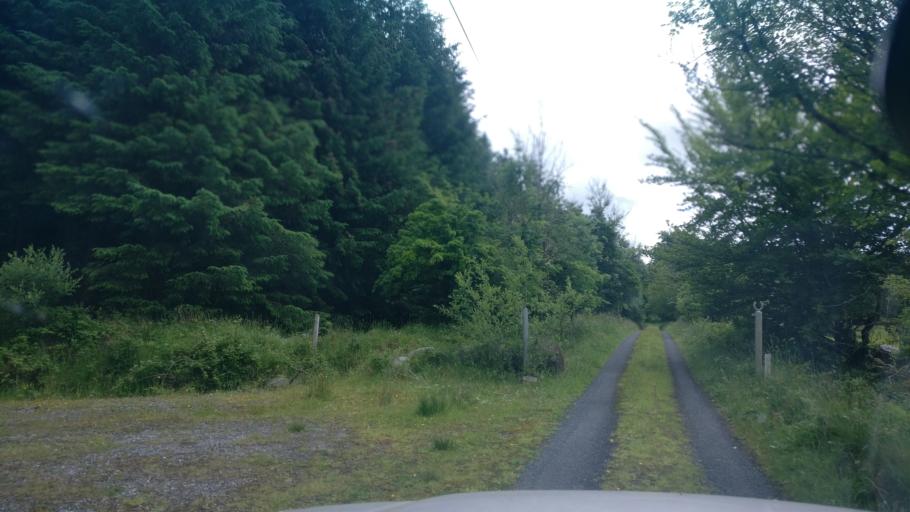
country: IE
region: Connaught
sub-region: County Galway
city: Loughrea
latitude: 53.1511
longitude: -8.5765
